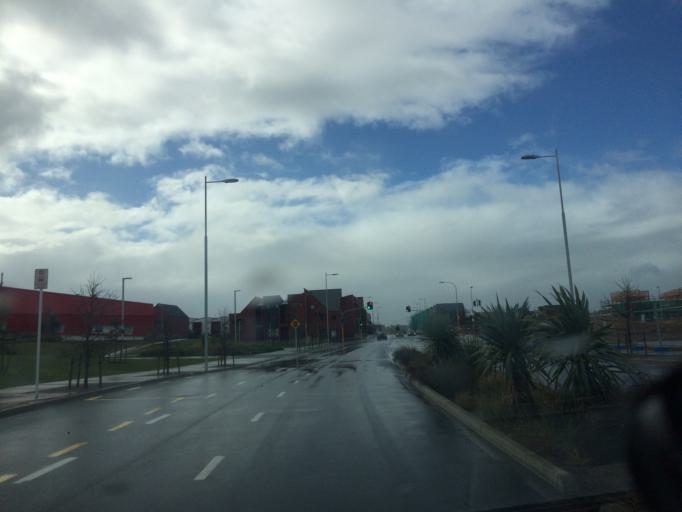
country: NZ
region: Auckland
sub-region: Auckland
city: Rosebank
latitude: -36.7954
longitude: 174.6555
